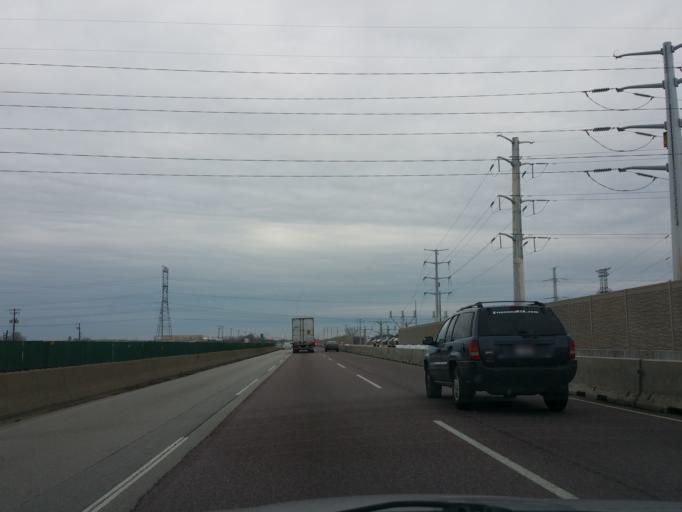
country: US
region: Illinois
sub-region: Kane County
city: East Dundee
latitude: 42.0664
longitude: -88.2426
